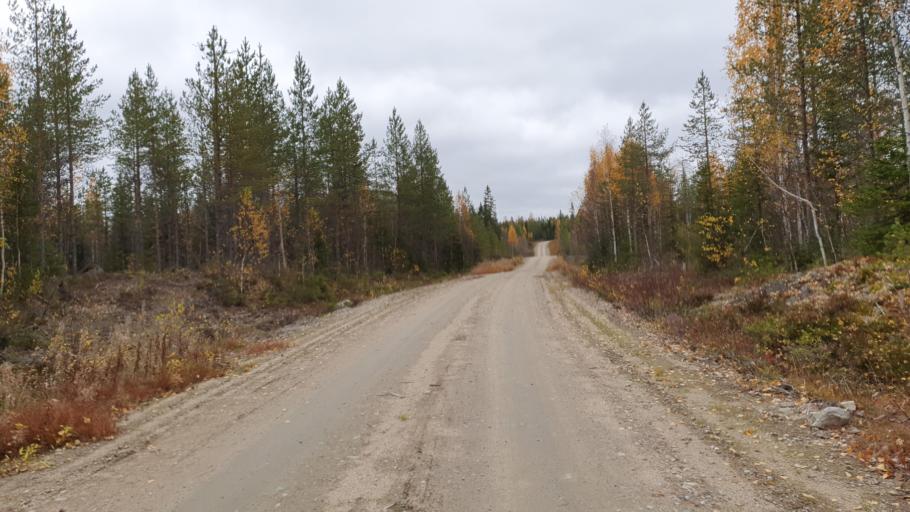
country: FI
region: Kainuu
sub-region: Kehys-Kainuu
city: Kuhmo
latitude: 64.4561
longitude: 29.6054
